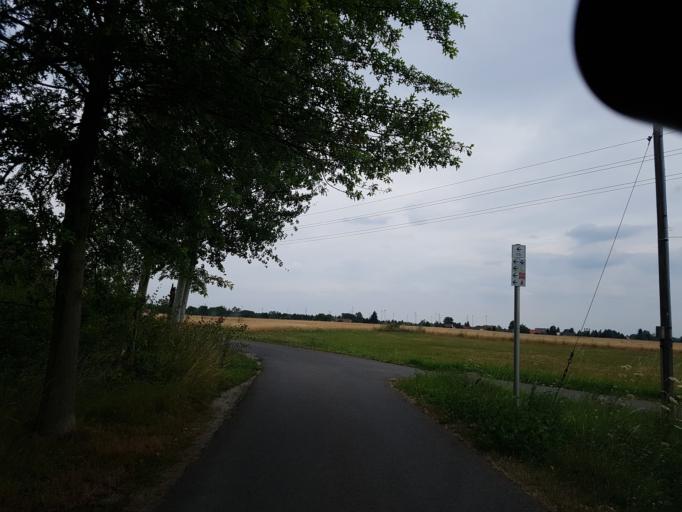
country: DE
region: Brandenburg
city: Sallgast
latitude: 51.5833
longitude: 13.8559
